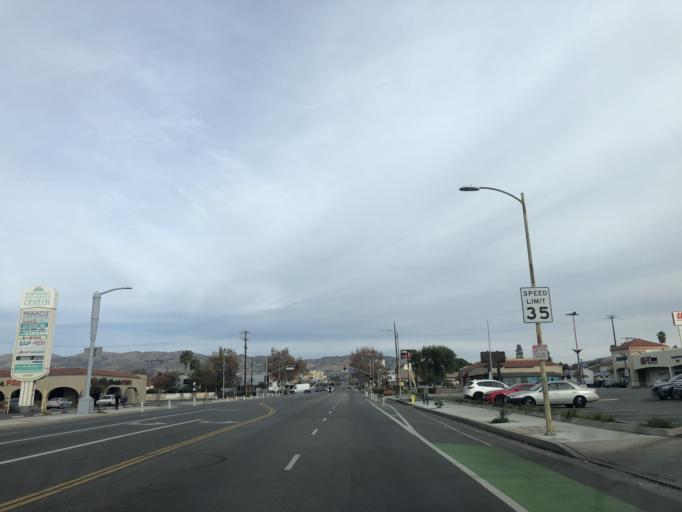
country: US
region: California
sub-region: Los Angeles County
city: Northridge
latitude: 34.2359
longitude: -118.5360
